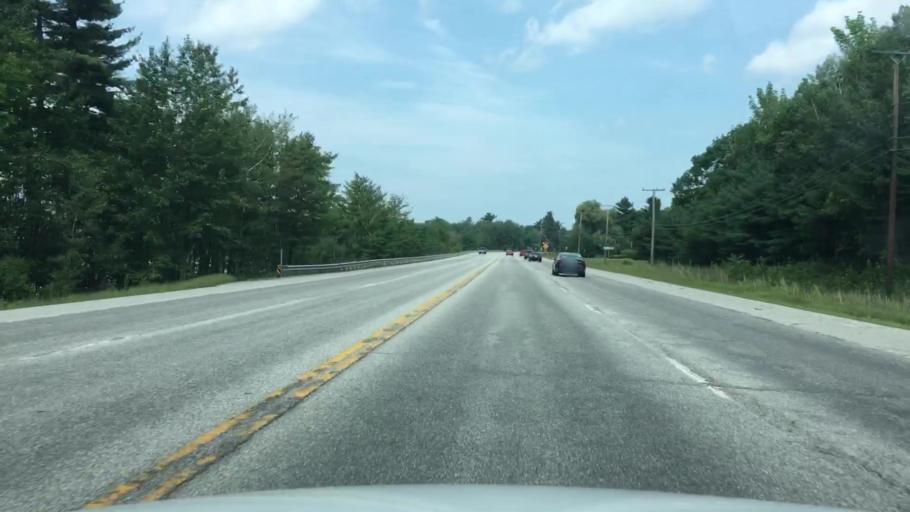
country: US
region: Maine
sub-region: Androscoggin County
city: Auburn
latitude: 44.1511
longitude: -70.2313
